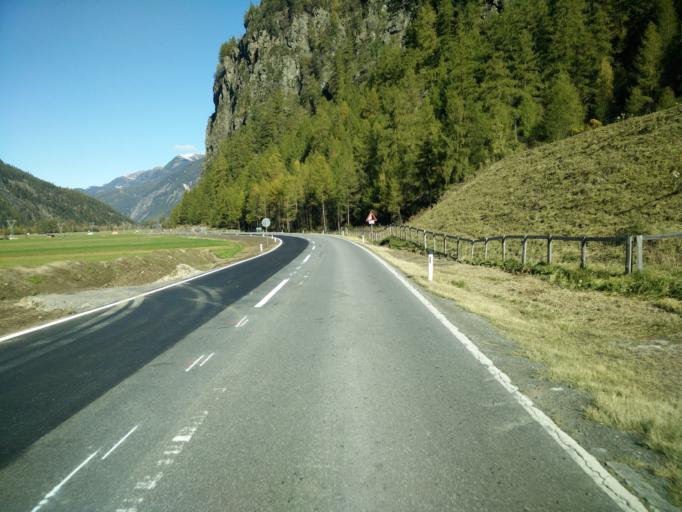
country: AT
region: Tyrol
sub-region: Politischer Bezirk Imst
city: Umhausen
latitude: 47.0524
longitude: 10.9661
